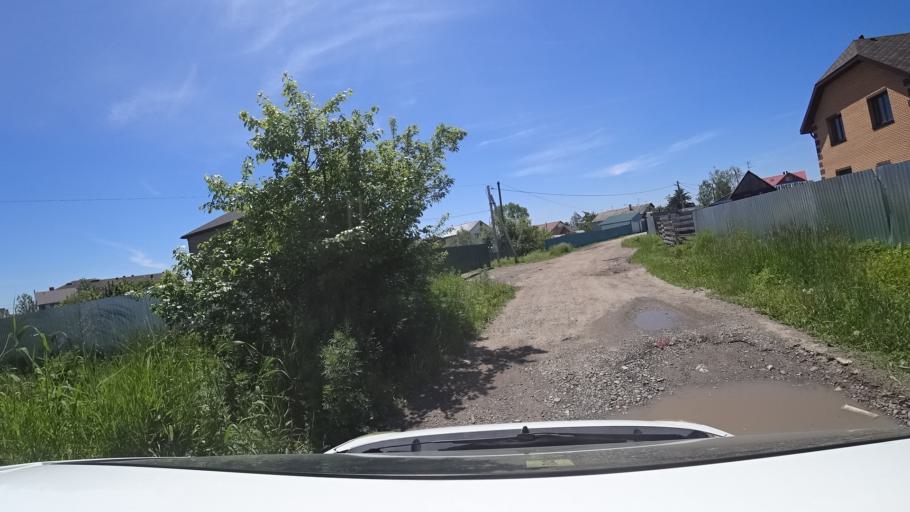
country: RU
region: Khabarovsk Krai
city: Topolevo
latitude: 48.5106
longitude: 135.1837
